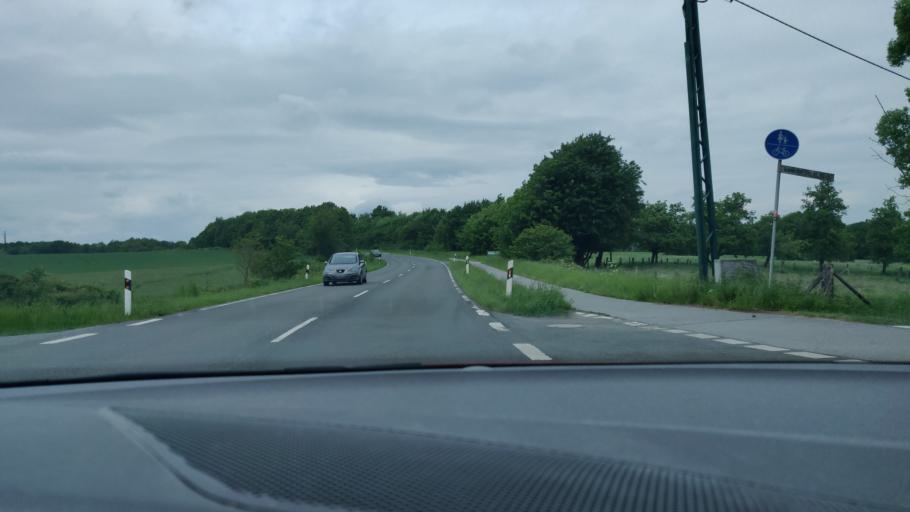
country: DE
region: North Rhine-Westphalia
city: Wulfrath
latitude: 51.2982
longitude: 7.0745
